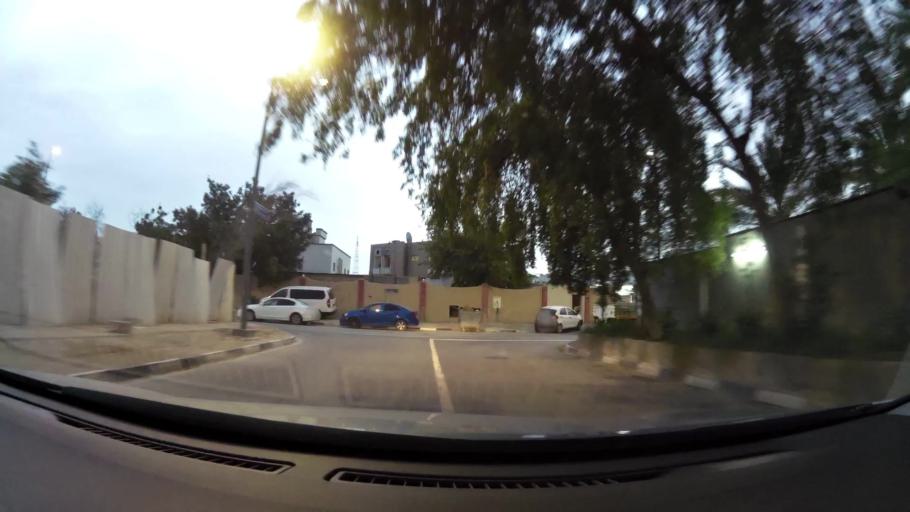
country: QA
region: Baladiyat ad Dawhah
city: Doha
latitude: 25.3429
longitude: 51.5122
